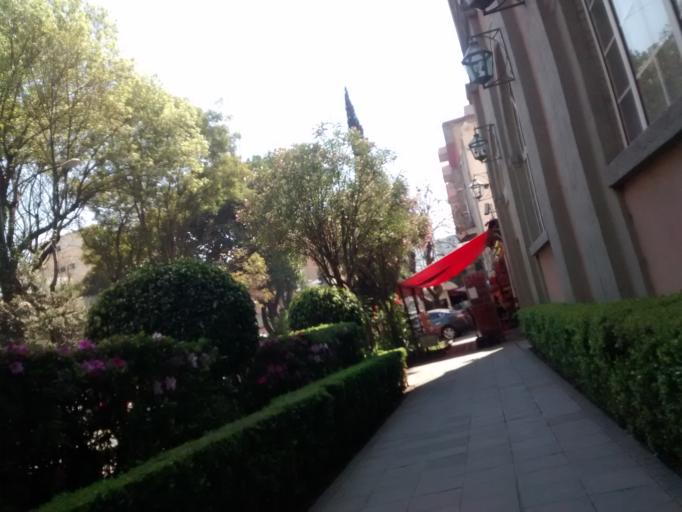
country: MX
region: Mexico City
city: Polanco
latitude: 19.4227
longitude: -99.1737
